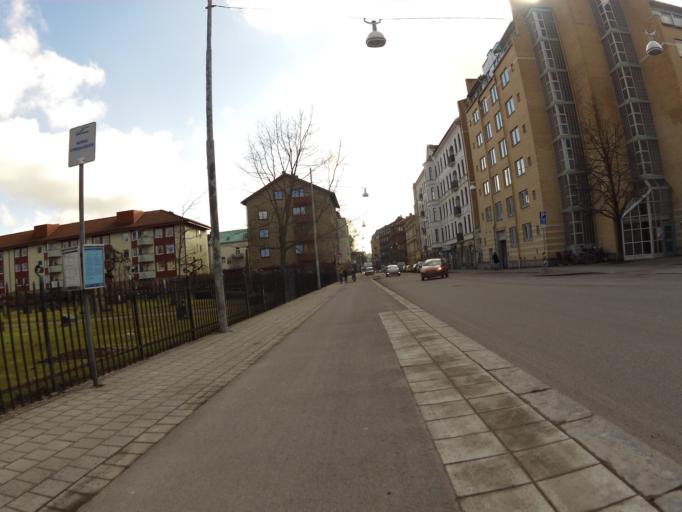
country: SE
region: Halland
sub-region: Halmstads Kommun
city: Halmstad
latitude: 56.6805
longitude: 12.8575
